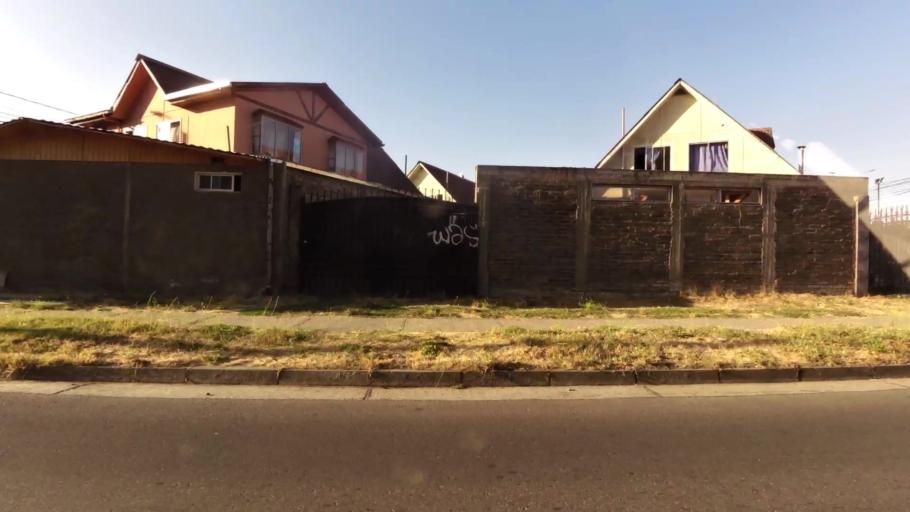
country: CL
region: Maule
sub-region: Provincia de Talca
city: Talca
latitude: -35.4517
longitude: -71.6695
